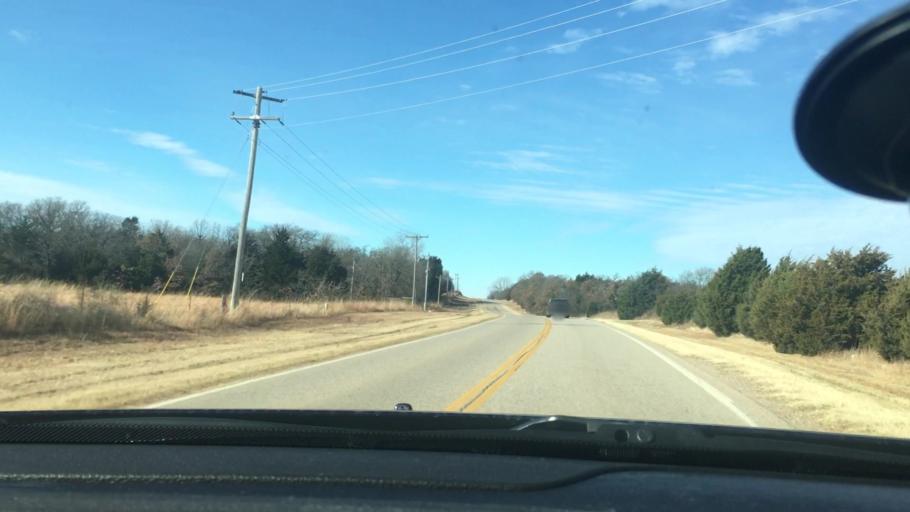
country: US
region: Oklahoma
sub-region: Garvin County
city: Stratford
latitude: 35.0147
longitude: -97.0747
